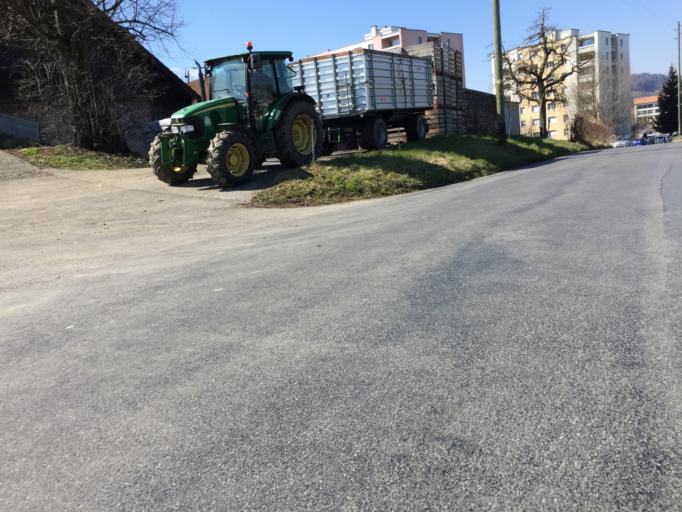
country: CH
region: Bern
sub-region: Bern-Mittelland District
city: Worb
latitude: 46.9228
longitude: 7.5722
